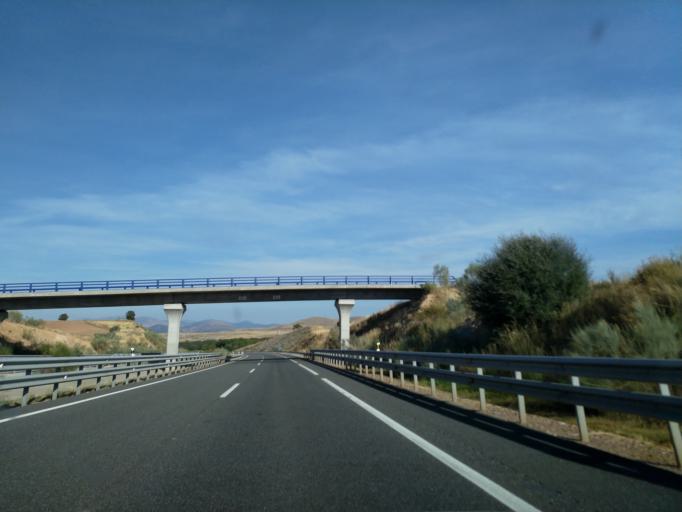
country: ES
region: Castille and Leon
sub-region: Provincia de Segovia
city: Villacastin
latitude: 40.7511
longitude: -4.4653
